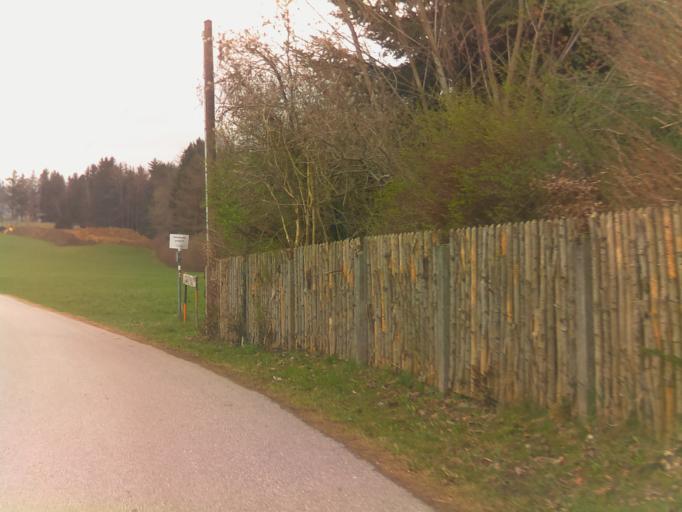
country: DE
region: Bavaria
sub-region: Upper Bavaria
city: Peissenberg
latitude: 47.8032
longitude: 11.0502
